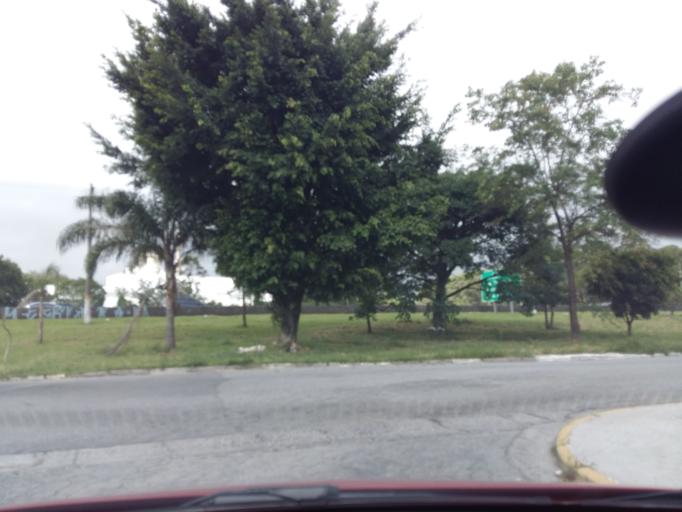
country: BR
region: Sao Paulo
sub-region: Sao Caetano Do Sul
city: Sao Caetano do Sul
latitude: -23.6393
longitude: -46.5928
